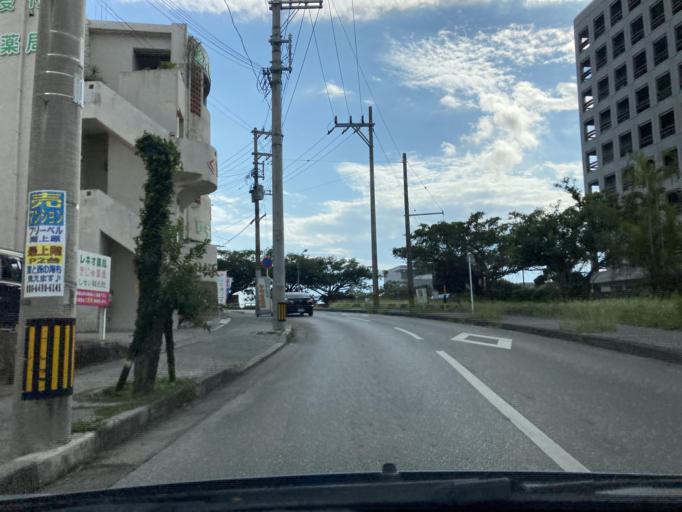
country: JP
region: Okinawa
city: Ginowan
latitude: 26.2419
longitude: 127.7609
